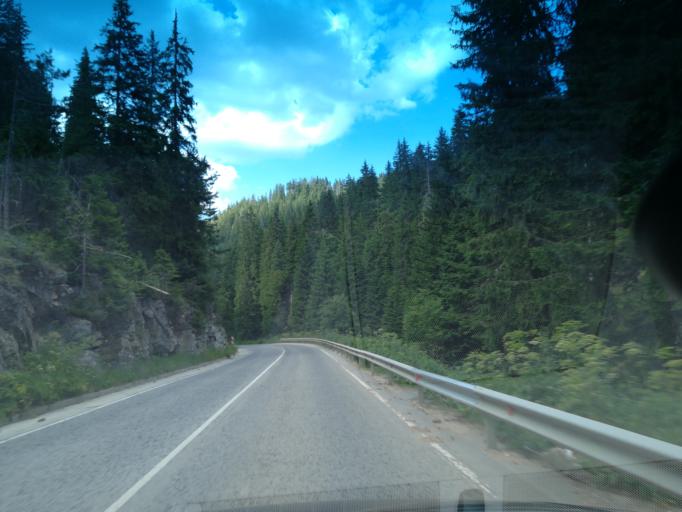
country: BG
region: Smolyan
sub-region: Obshtina Chepelare
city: Chepelare
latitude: 41.6633
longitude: 24.7139
